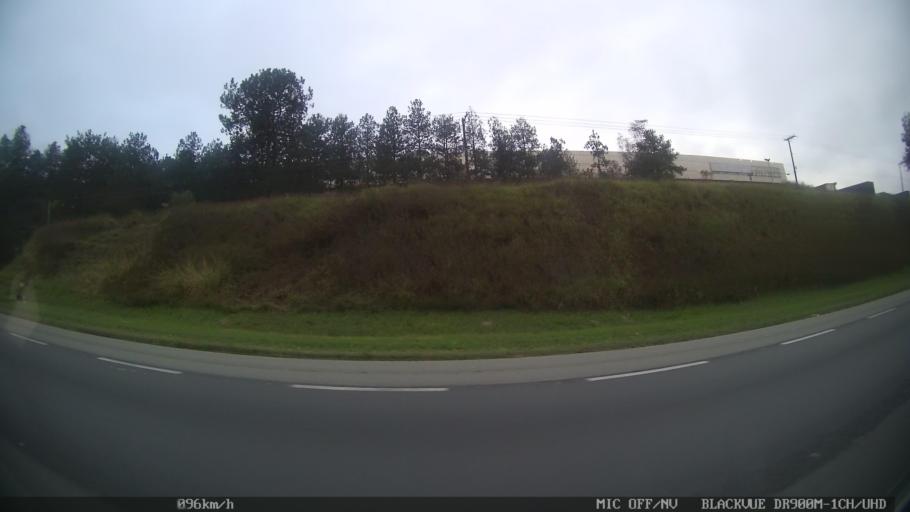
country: BR
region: Sao Paulo
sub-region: Itapecerica Da Serra
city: Itapecerica da Serra
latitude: -23.7106
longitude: -46.8767
